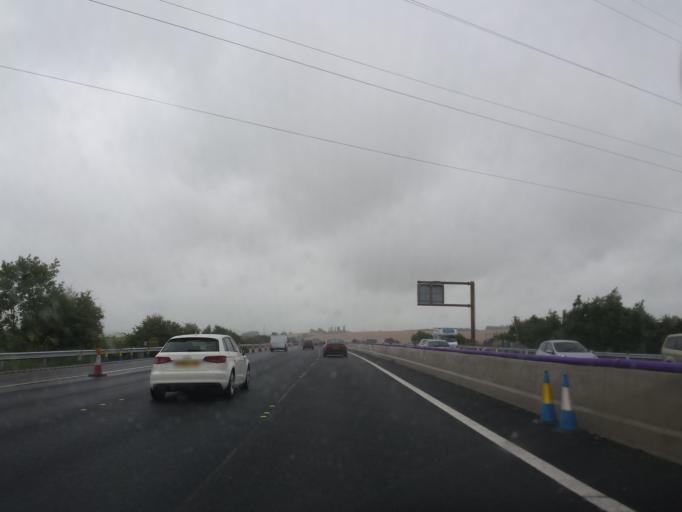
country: GB
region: England
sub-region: Derbyshire
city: Bolsover
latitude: 53.2293
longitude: -1.3324
